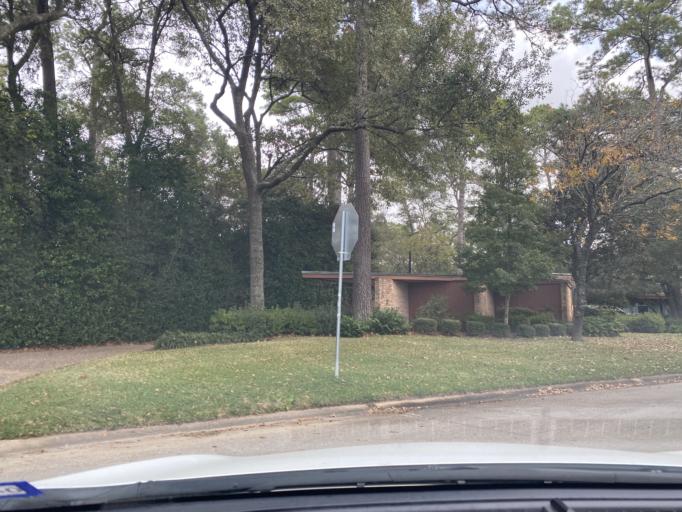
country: US
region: Texas
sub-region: Harris County
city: Hunters Creek Village
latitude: 29.7685
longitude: -95.4708
